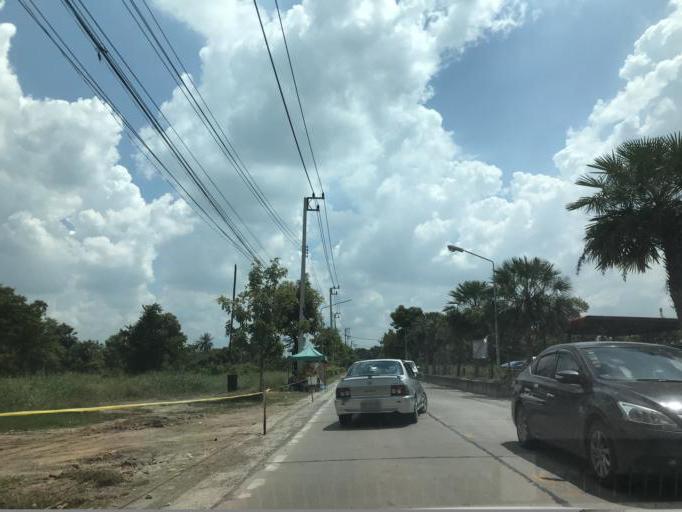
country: TH
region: Phra Nakhon Si Ayutthaya
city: Ban Bang Kadi Pathum Thani
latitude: 14.0066
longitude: 100.5421
